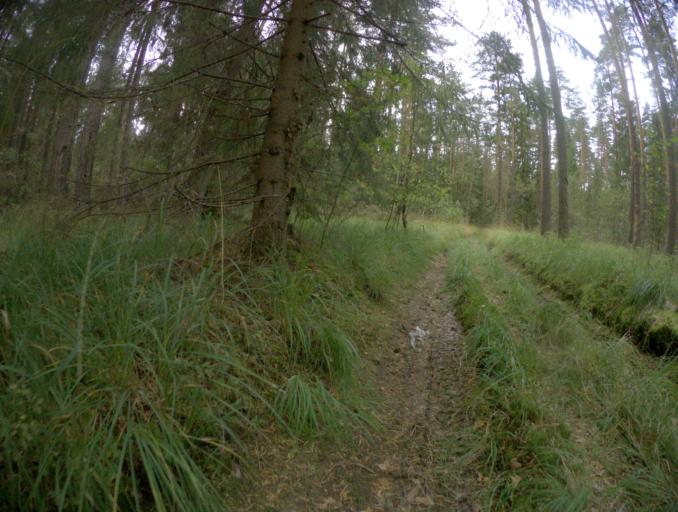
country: RU
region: Vladimir
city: Golovino
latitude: 55.8677
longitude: 40.3891
